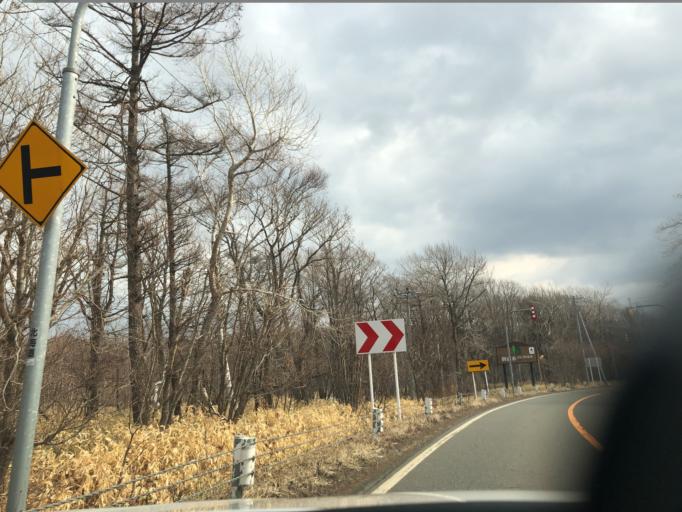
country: JP
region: Hokkaido
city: Chitose
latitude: 42.7633
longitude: 141.7291
